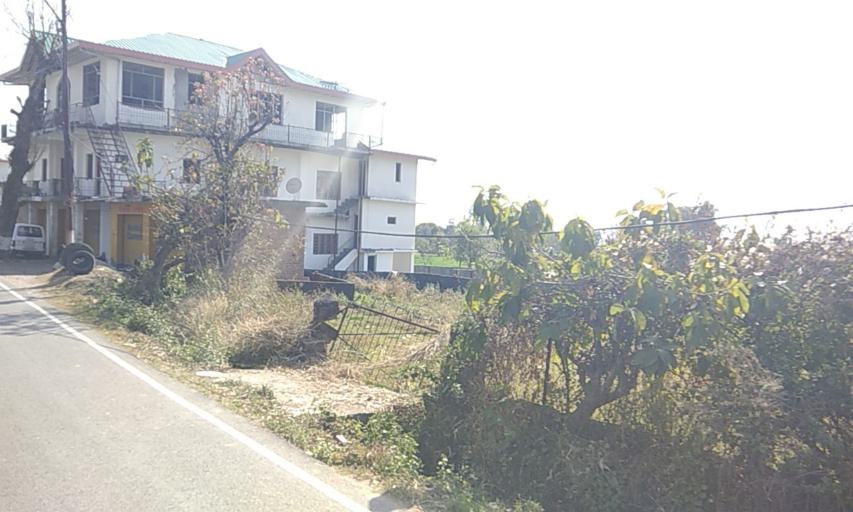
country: IN
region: Himachal Pradesh
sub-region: Kangra
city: Dharmsala
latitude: 32.1692
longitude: 76.3908
